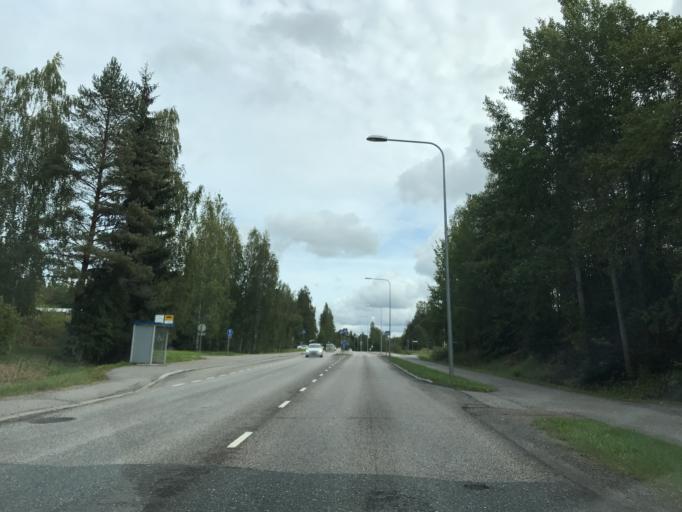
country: FI
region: Paijanne Tavastia
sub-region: Lahti
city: Lahti
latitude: 60.9899
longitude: 25.7399
